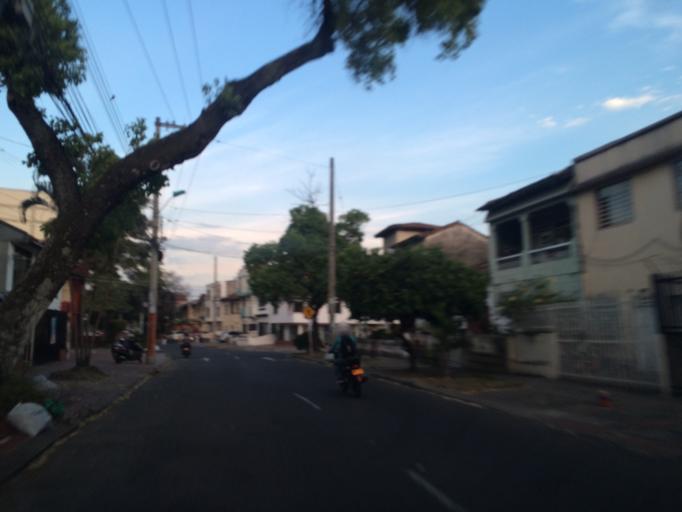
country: CO
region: Valle del Cauca
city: Cali
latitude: 3.4335
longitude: -76.5409
